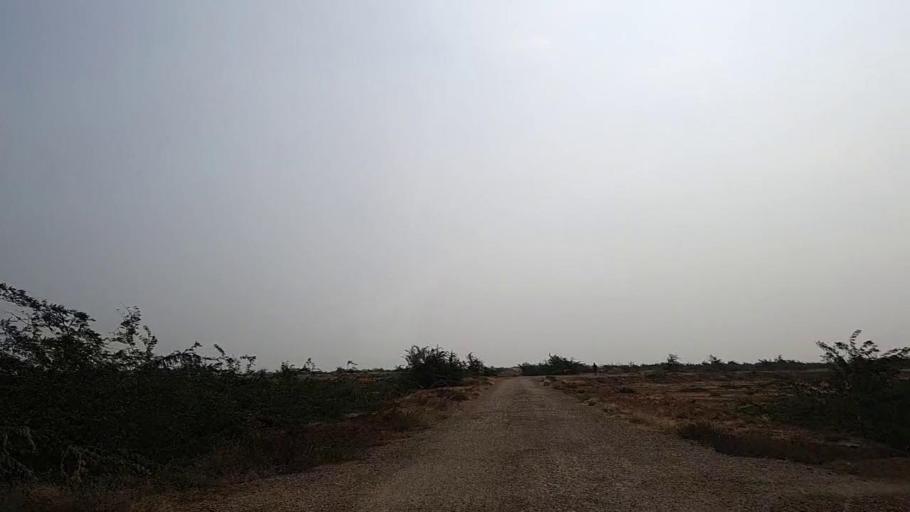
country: PK
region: Sindh
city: Thatta
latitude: 24.7259
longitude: 67.8328
